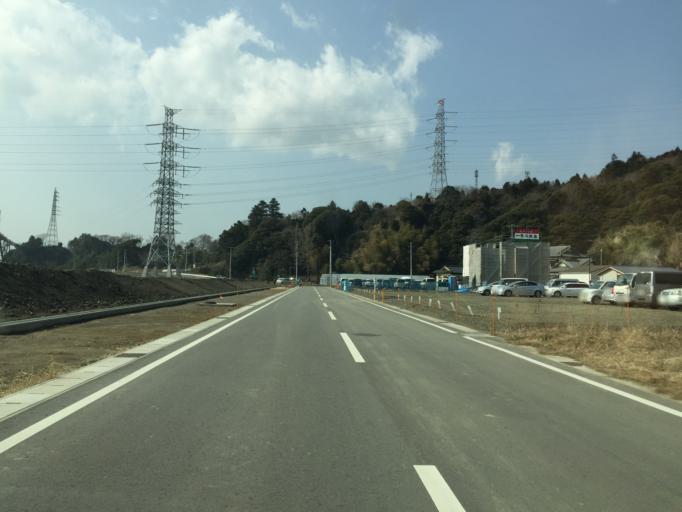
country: JP
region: Fukushima
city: Iwaki
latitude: 36.9154
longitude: 140.8232
